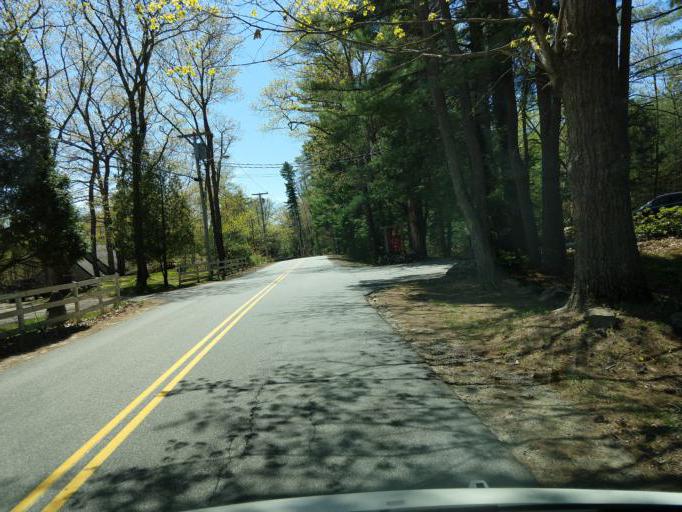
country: US
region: Maine
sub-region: York County
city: Cape Neddick
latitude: 43.2270
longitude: -70.6277
